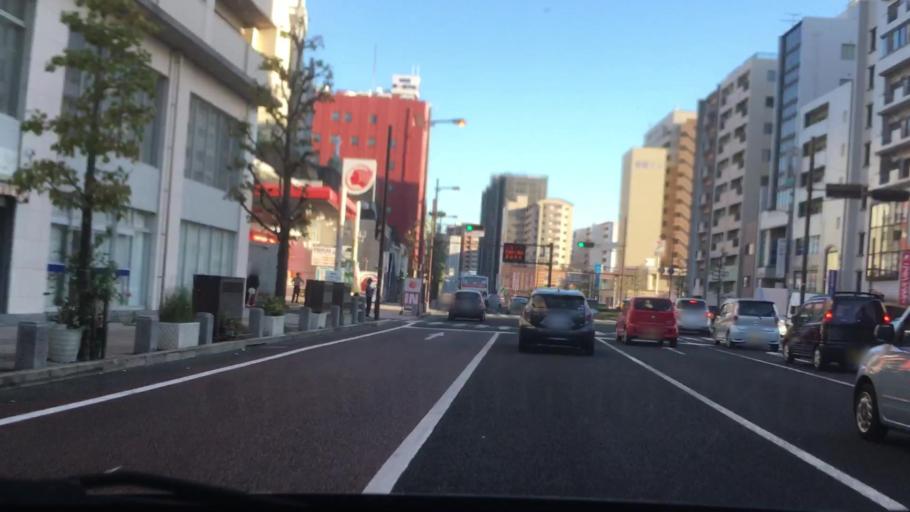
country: JP
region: Nagasaki
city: Sasebo
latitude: 33.1664
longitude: 129.7251
